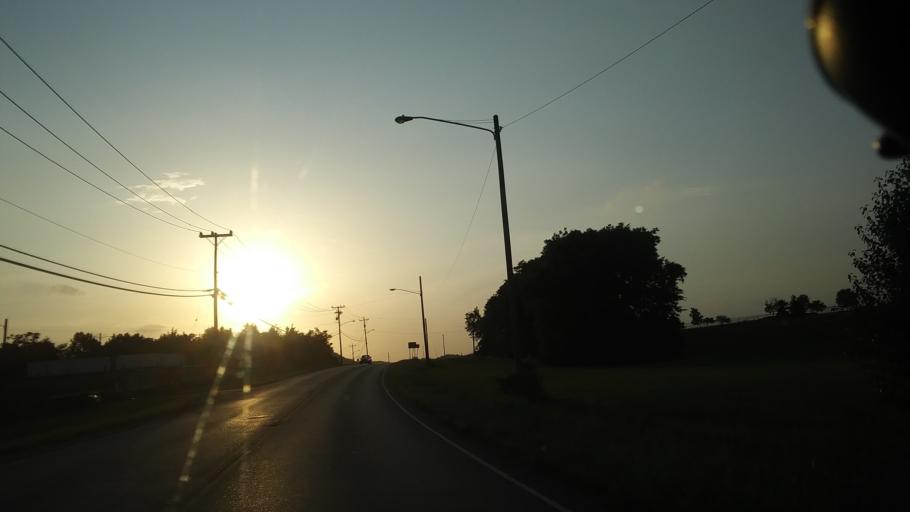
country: US
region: Tennessee
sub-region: Davidson County
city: Belle Meade
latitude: 36.1706
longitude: -86.8849
